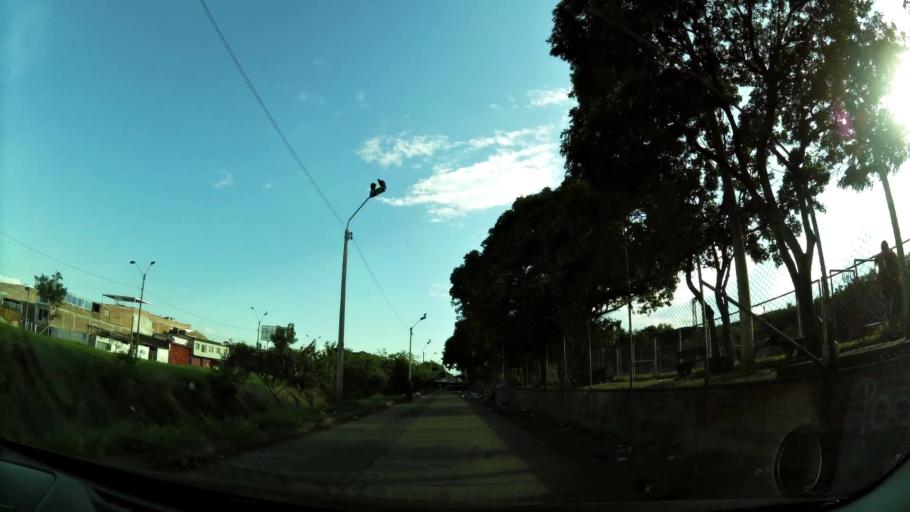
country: CO
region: Valle del Cauca
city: Cali
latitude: 3.4306
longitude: -76.5202
